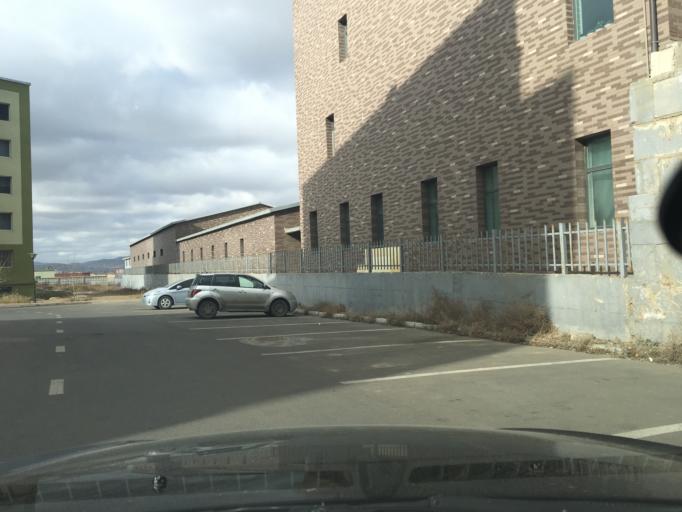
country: MN
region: Ulaanbaatar
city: Ulaanbaatar
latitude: 47.8790
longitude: 106.8487
